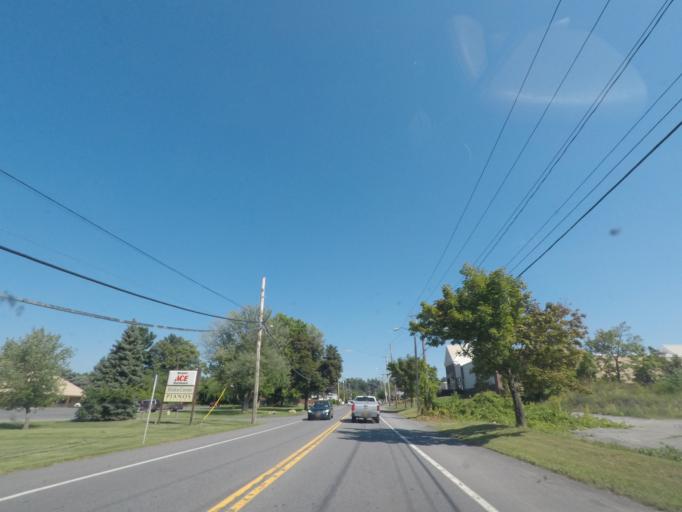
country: US
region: New York
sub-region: Albany County
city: West Albany
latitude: 42.7371
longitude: -73.7654
